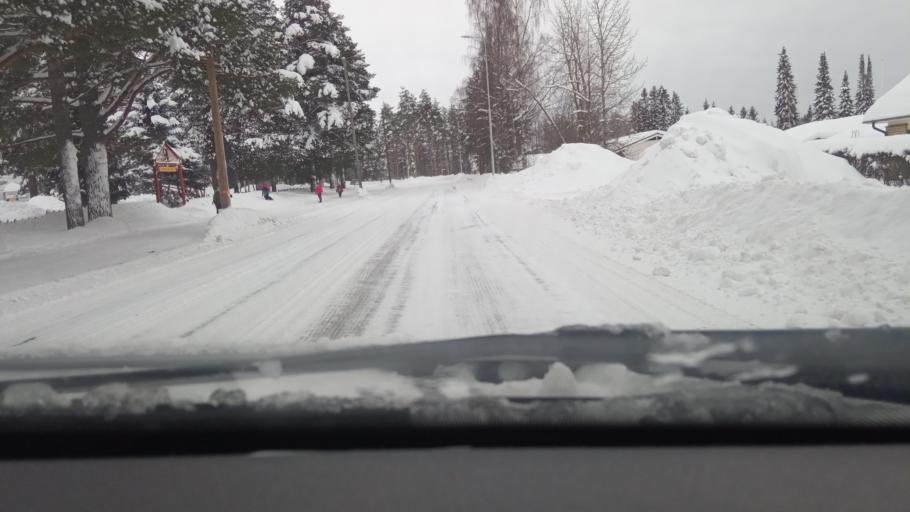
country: FI
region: Southern Ostrobothnia
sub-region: Jaerviseutu
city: Alajaervi
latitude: 62.9986
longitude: 23.8032
